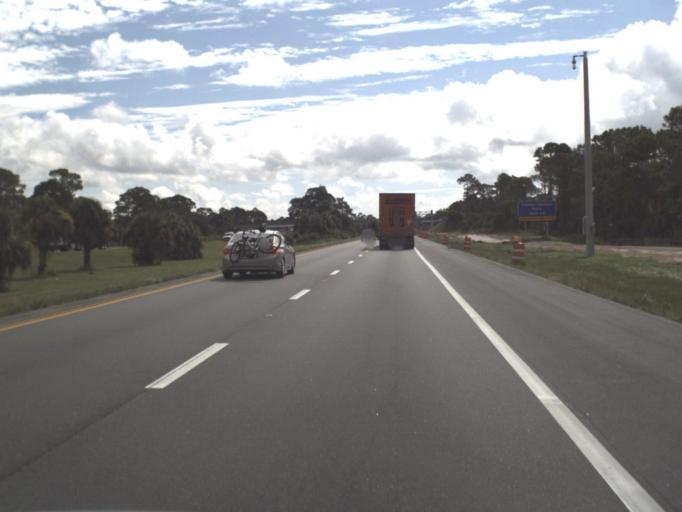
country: US
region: Florida
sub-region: Sarasota County
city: Warm Mineral Springs
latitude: 27.0995
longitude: -82.2372
